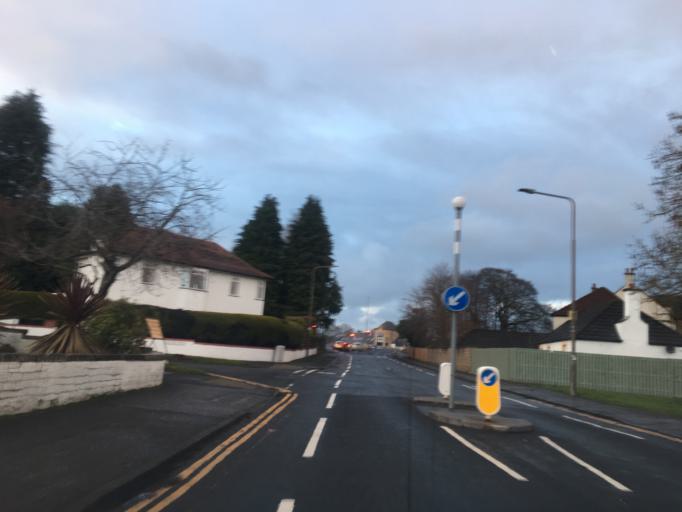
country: GB
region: Scotland
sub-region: Edinburgh
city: Colinton
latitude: 55.9615
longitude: -3.2717
